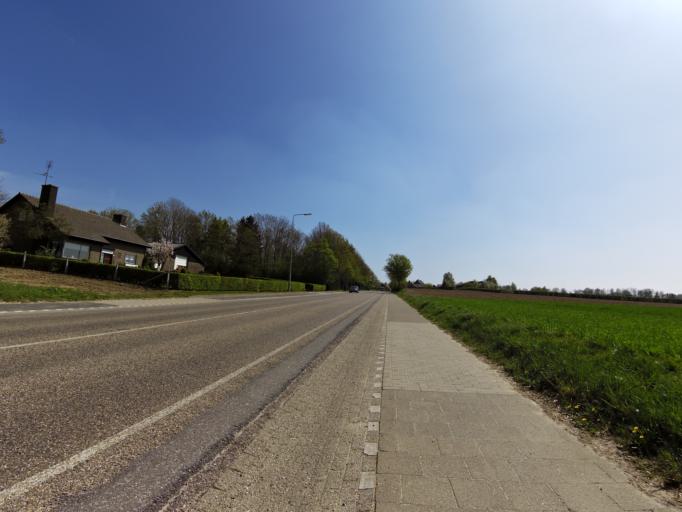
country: NL
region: Limburg
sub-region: Gemeente Voerendaal
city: Ubachsberg
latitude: 50.8585
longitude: 5.9420
